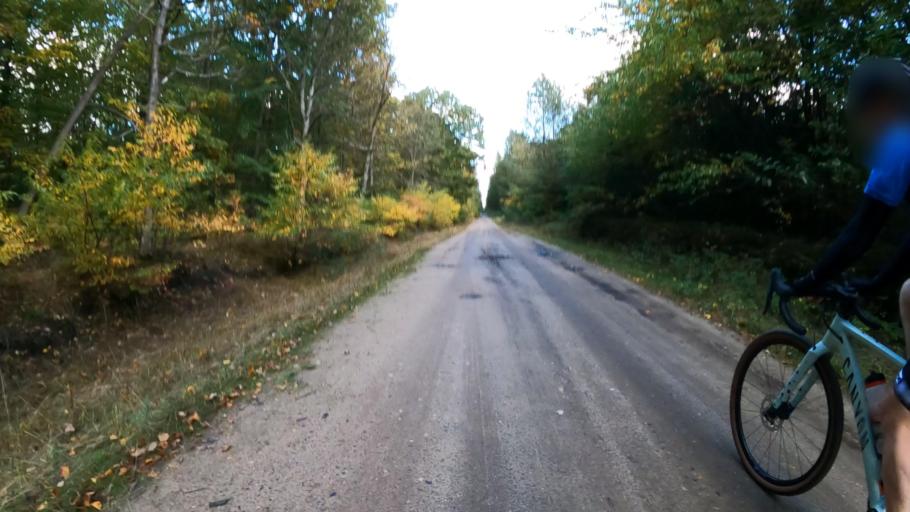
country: DE
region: Schleswig-Holstein
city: Heidmuhlen
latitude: 53.9380
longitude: 10.0835
